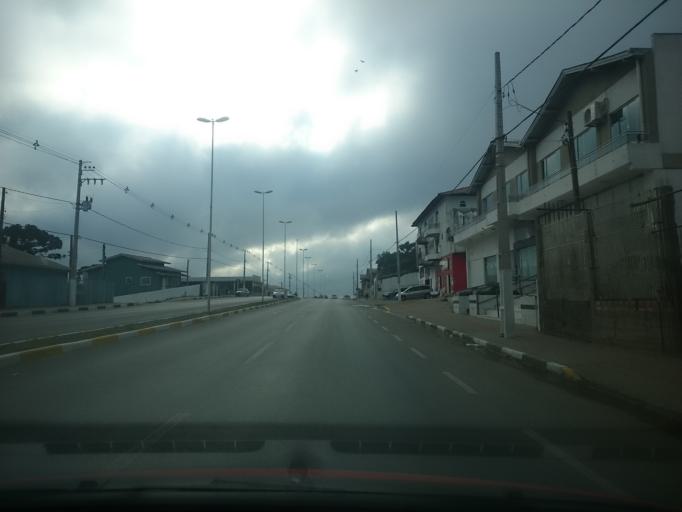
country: BR
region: Santa Catarina
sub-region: Lages
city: Lages
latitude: -27.8305
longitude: -50.3424
